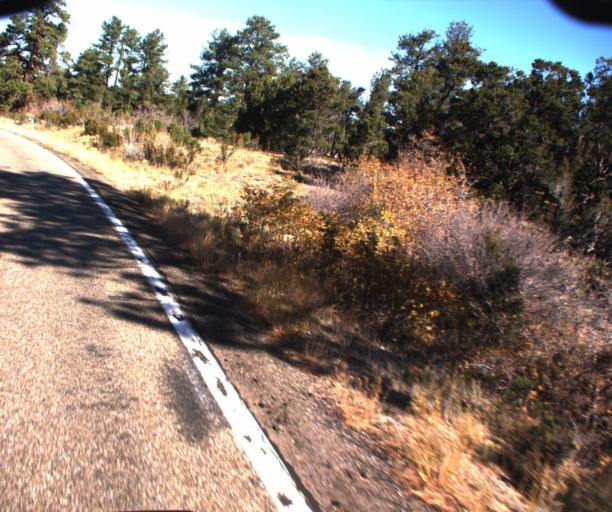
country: US
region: Arizona
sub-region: Coconino County
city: Fredonia
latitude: 36.7881
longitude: -112.2574
